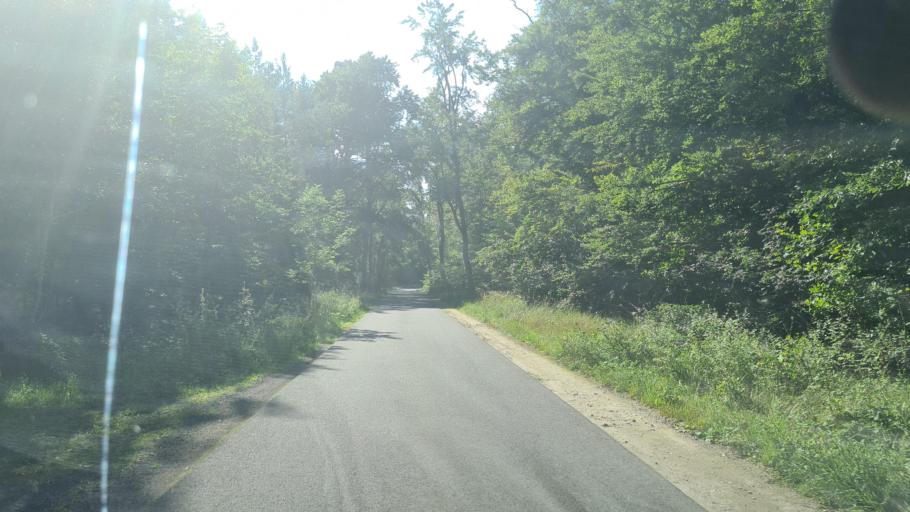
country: DE
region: Brandenburg
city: Brieselang
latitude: 52.6389
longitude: 12.9622
